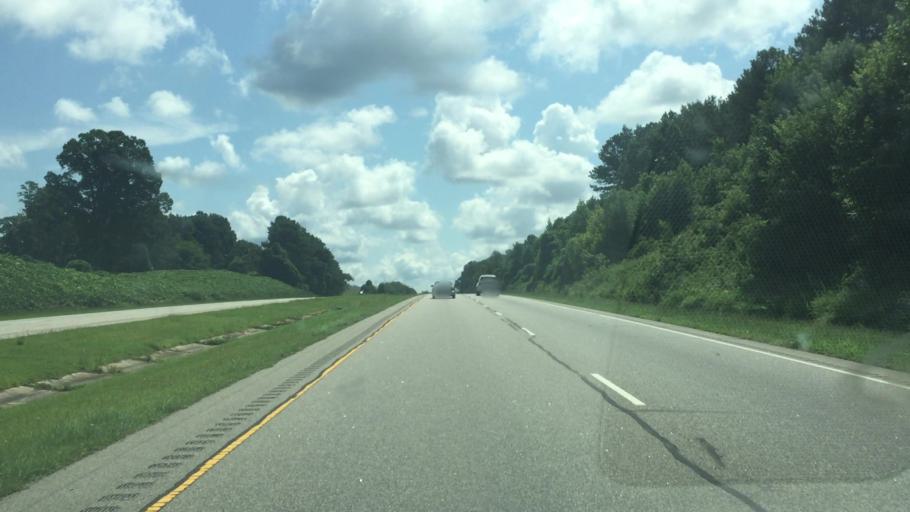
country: US
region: North Carolina
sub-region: Anson County
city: Wadesboro
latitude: 34.9628
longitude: -79.9999
